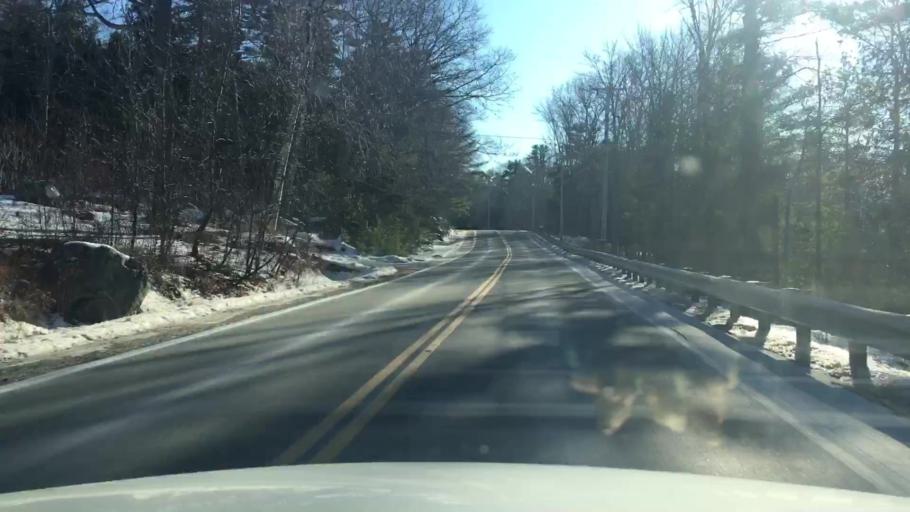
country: US
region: Maine
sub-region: Hancock County
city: Orland
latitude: 44.5402
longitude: -68.7456
